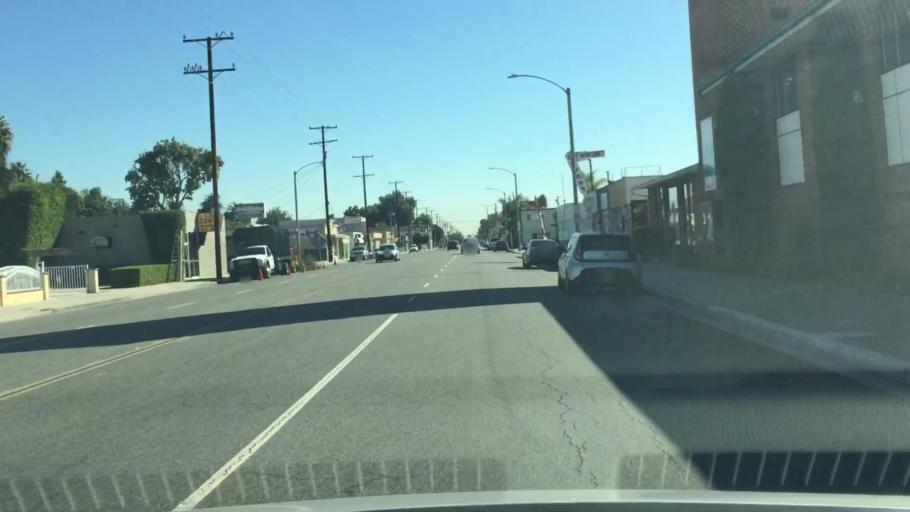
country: US
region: California
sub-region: Los Angeles County
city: Paramount
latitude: 33.8601
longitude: -118.1839
